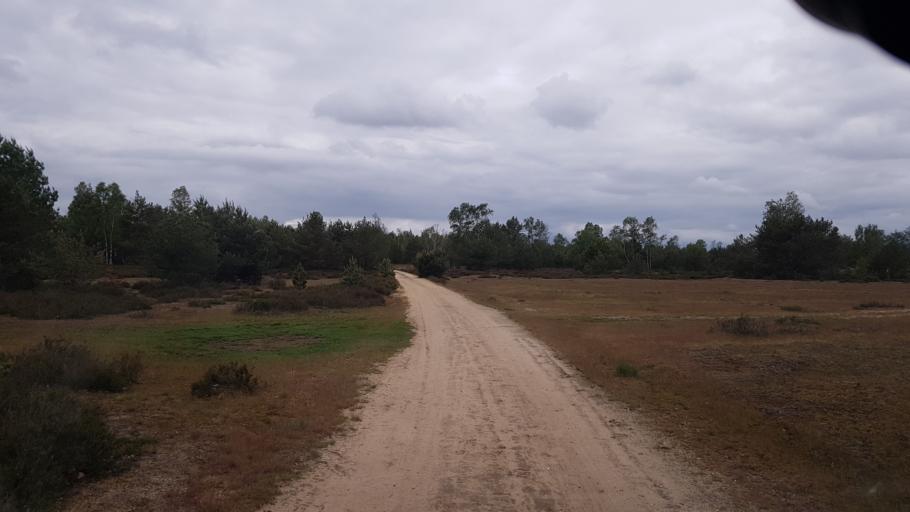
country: DE
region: Brandenburg
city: Hohenleipisch
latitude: 51.5102
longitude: 13.5062
